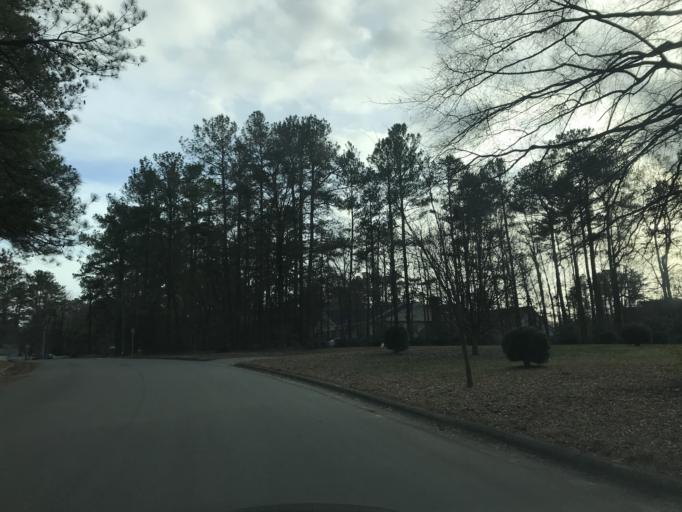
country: US
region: North Carolina
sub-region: Wake County
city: Raleigh
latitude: 35.7965
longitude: -78.6179
